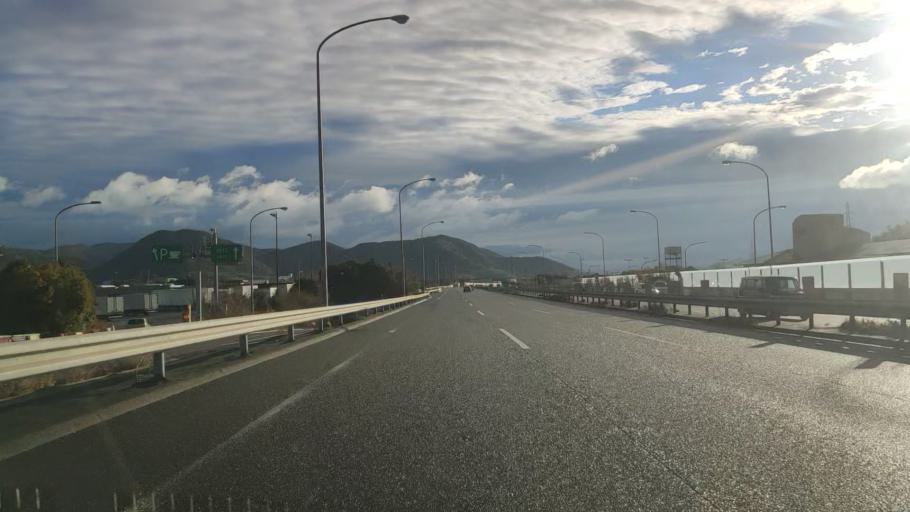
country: JP
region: Hyogo
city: Shirahamacho-usazakiminami
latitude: 34.8003
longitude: 134.7492
